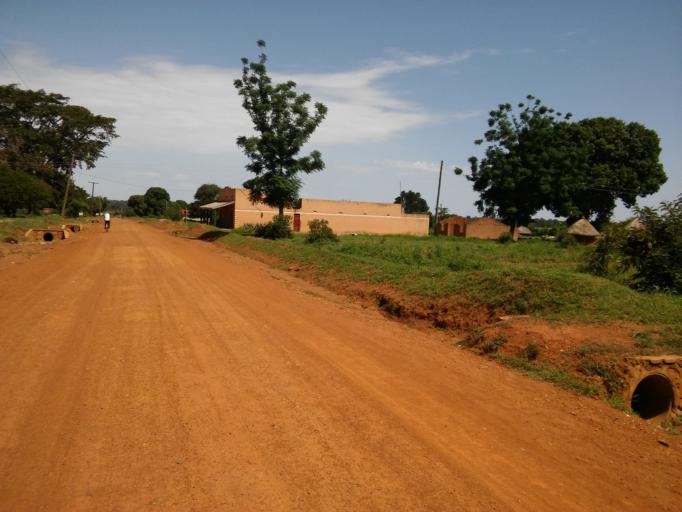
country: UG
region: Eastern Region
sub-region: Kumi District
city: Kumi
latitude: 1.4861
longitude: 33.9234
